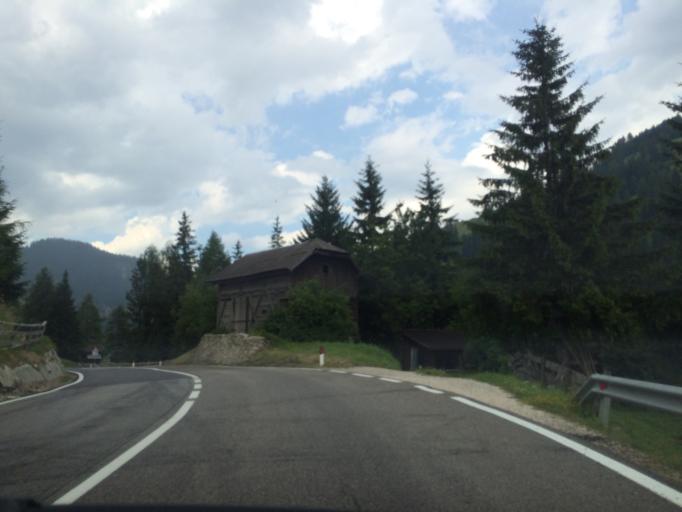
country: IT
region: Trentino-Alto Adige
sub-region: Bolzano
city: Badia
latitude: 46.6153
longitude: 11.8938
